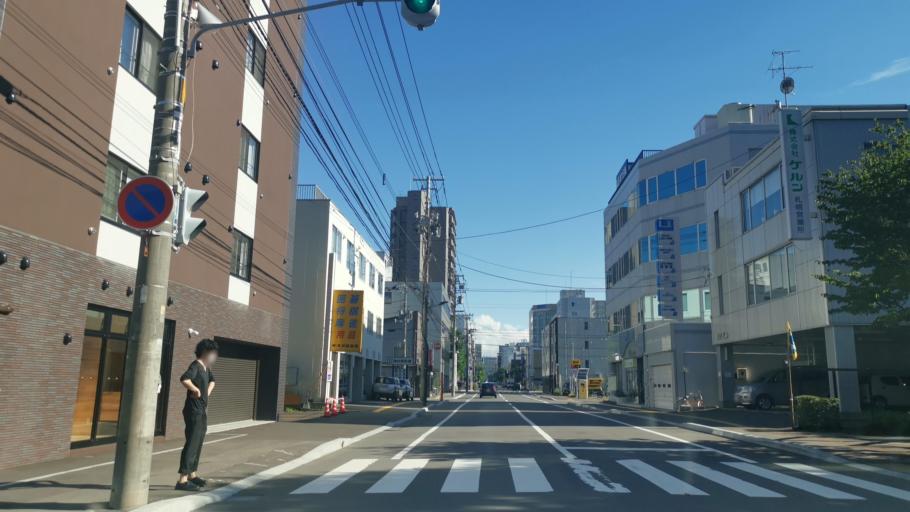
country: JP
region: Hokkaido
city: Sapporo
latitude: 43.0806
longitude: 141.3471
